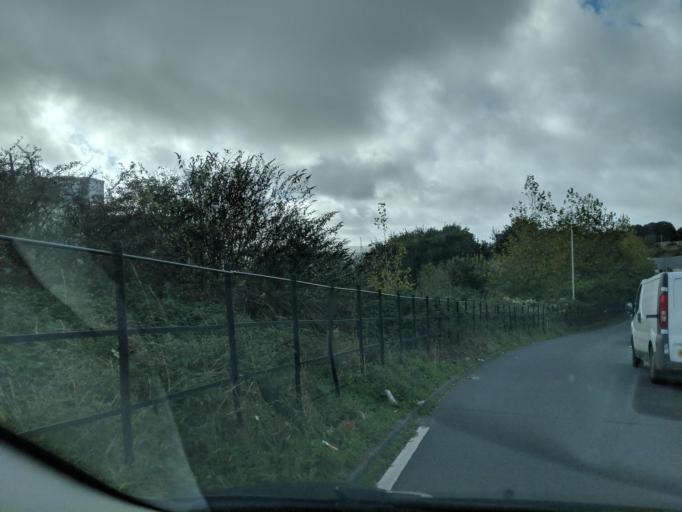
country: GB
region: England
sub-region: Cornwall
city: Torpoint
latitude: 50.3978
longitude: -4.1861
